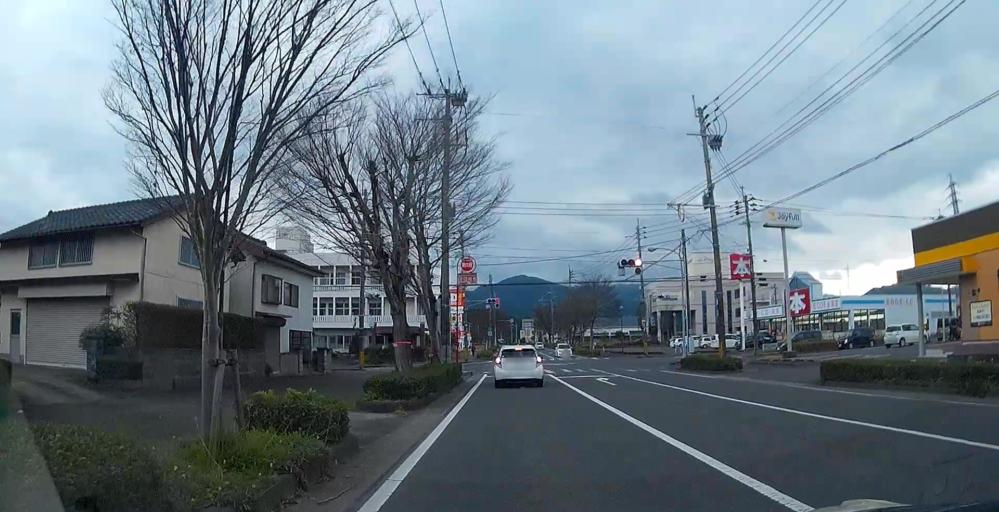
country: JP
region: Kagoshima
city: Izumi
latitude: 32.0748
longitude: 130.3478
